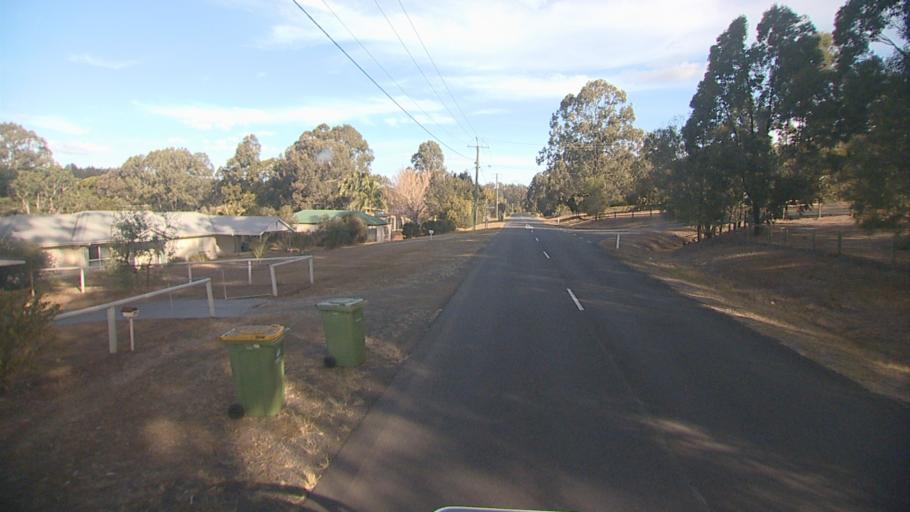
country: AU
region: Queensland
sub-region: Logan
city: Cedar Vale
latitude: -27.8757
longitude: 153.0107
